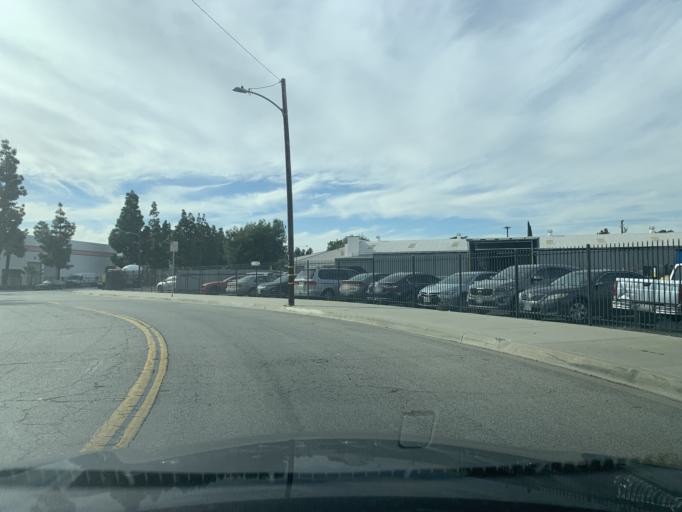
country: US
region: California
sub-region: Los Angeles County
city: South El Monte
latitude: 34.0735
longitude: -118.0497
